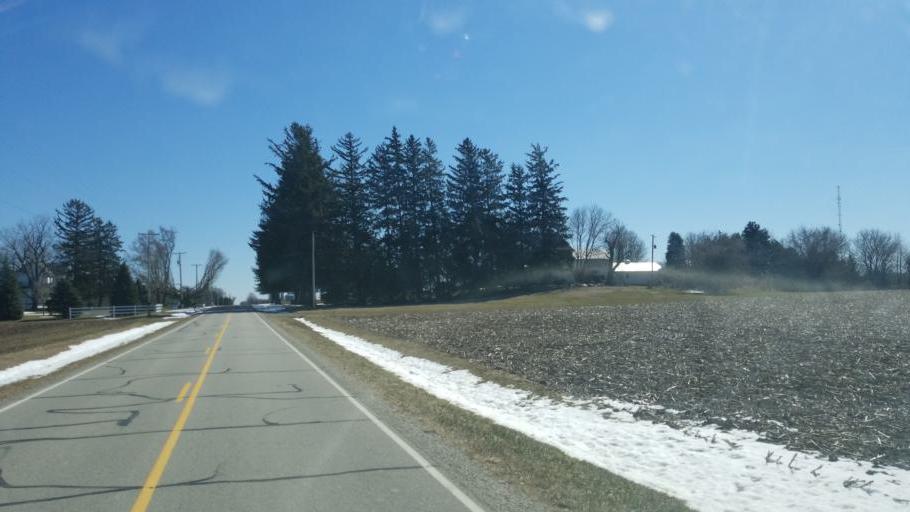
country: US
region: Ohio
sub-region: Crawford County
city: Bucyrus
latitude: 40.8047
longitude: -83.0594
